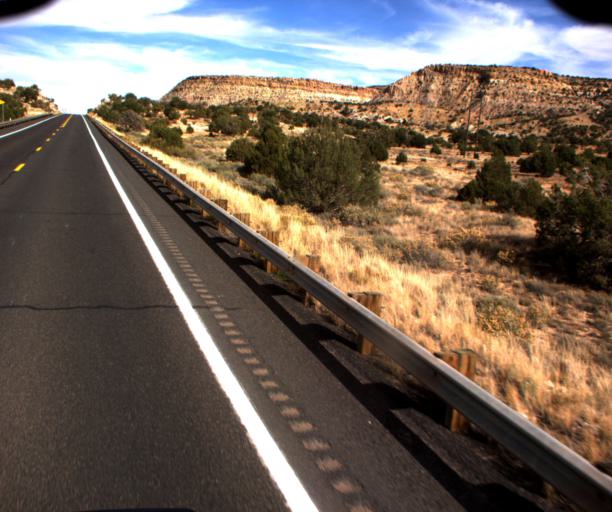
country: US
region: Arizona
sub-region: Navajo County
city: Kayenta
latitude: 36.6819
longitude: -110.3843
